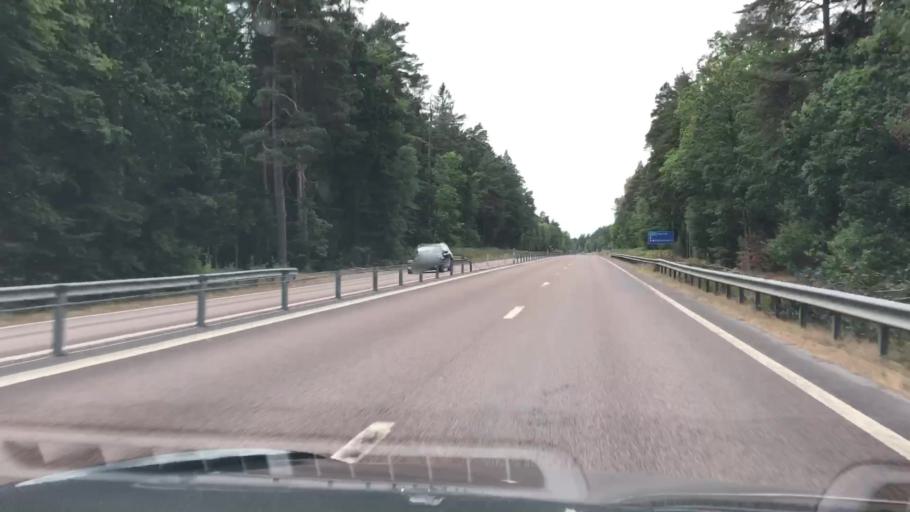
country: SE
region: Kalmar
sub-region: Torsas Kommun
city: Torsas
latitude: 56.2921
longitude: 15.9919
